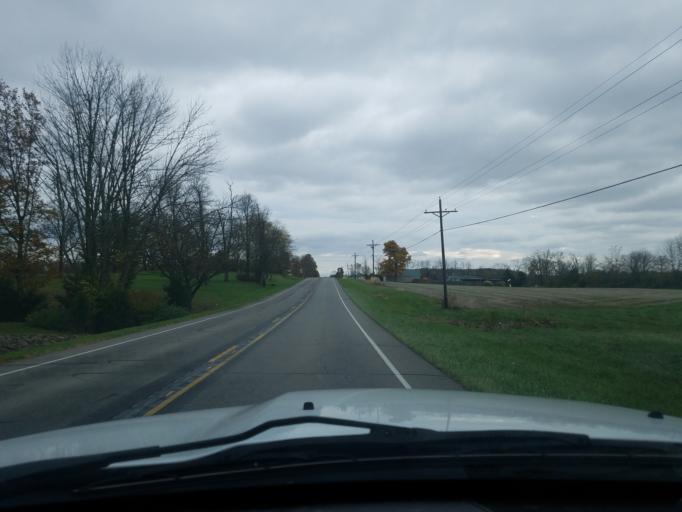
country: US
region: Indiana
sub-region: Bartholomew County
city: Hope
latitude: 39.2565
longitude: -85.7716
